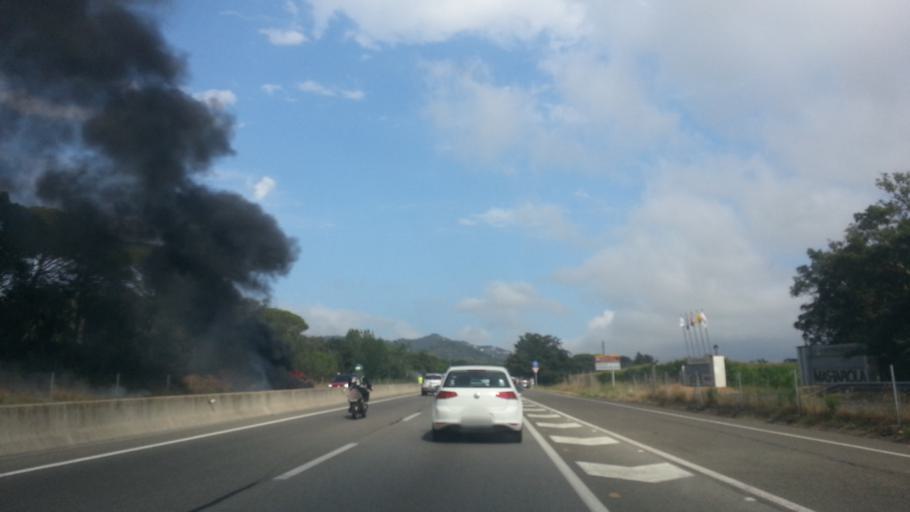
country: ES
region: Catalonia
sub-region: Provincia de Girona
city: Santa Cristina d'Aro
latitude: 41.8275
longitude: 2.9655
